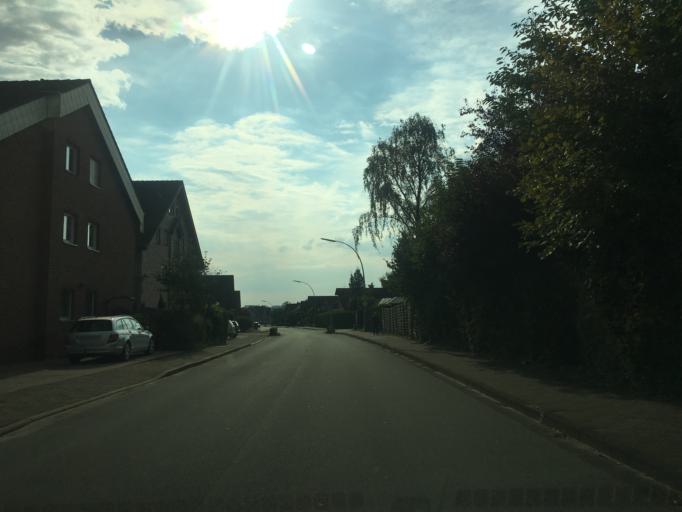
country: DE
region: North Rhine-Westphalia
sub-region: Regierungsbezirk Munster
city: Nordkirchen
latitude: 51.7077
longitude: 7.5425
